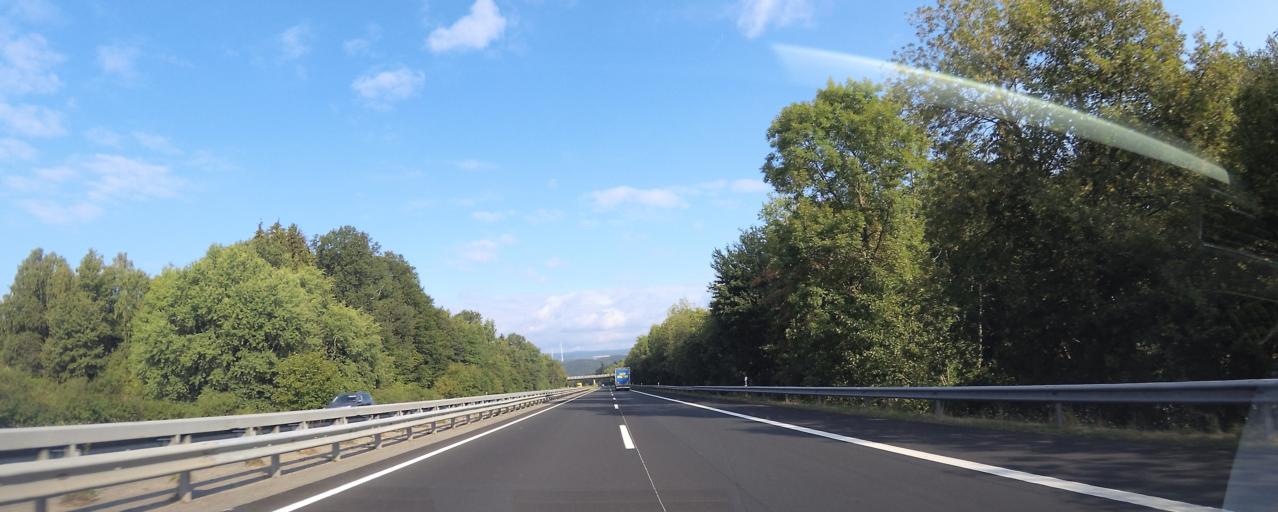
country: DE
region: Rheinland-Pfalz
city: Gimbweiler
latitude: 49.5946
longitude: 7.1938
